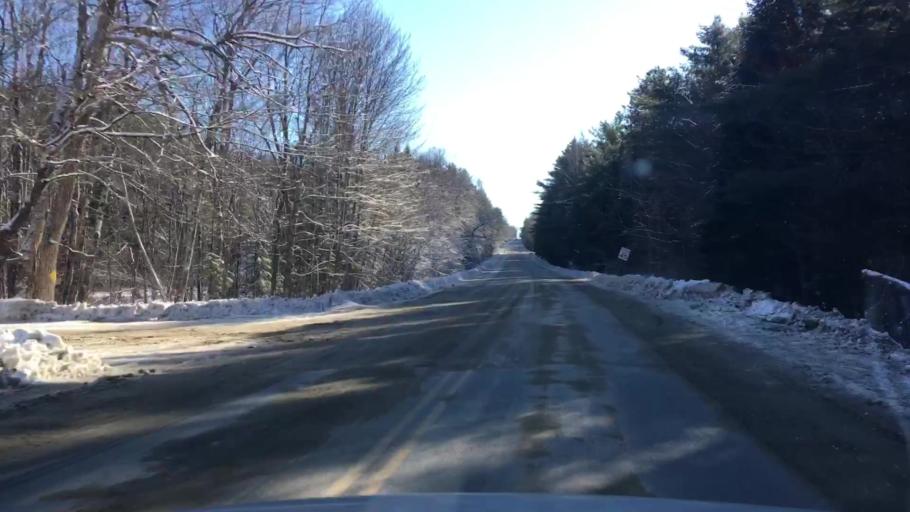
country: US
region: Maine
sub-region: Kennebec County
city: Readfield
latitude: 44.3545
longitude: -69.9914
